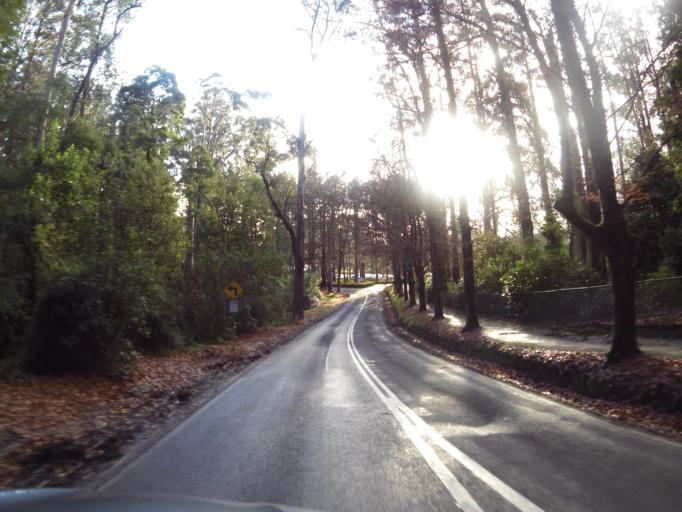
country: AU
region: Victoria
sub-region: Yarra Ranges
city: Kallista
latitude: -37.8769
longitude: 145.3564
